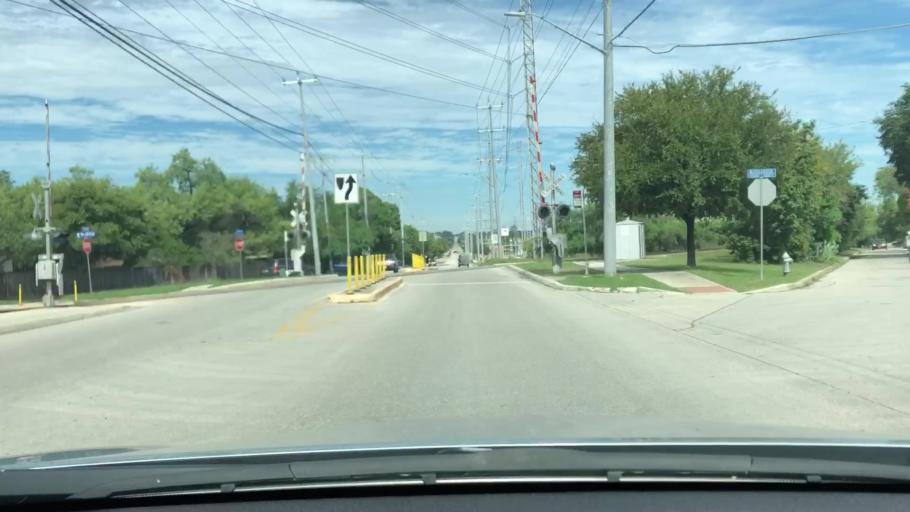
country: US
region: Texas
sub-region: Bexar County
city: Olmos Park
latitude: 29.4809
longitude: -98.4917
